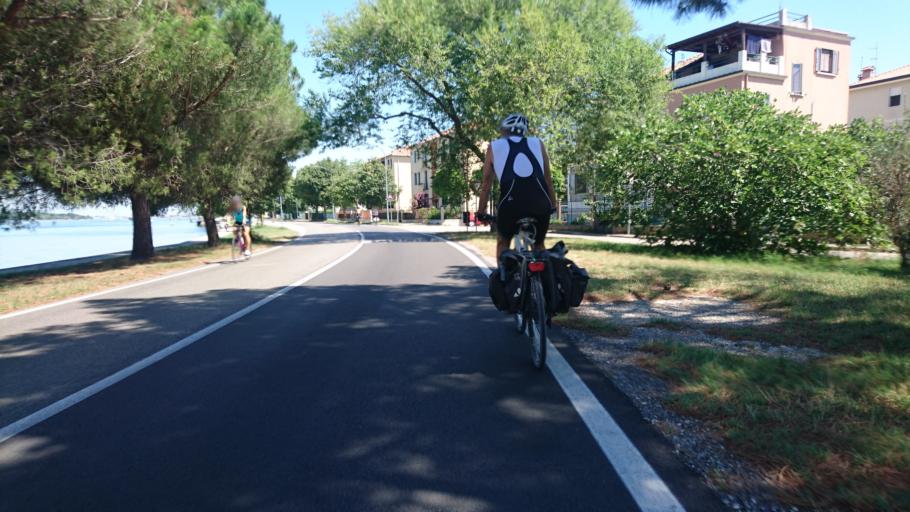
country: IT
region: Veneto
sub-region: Provincia di Venezia
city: Lido
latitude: 45.3690
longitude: 12.3367
